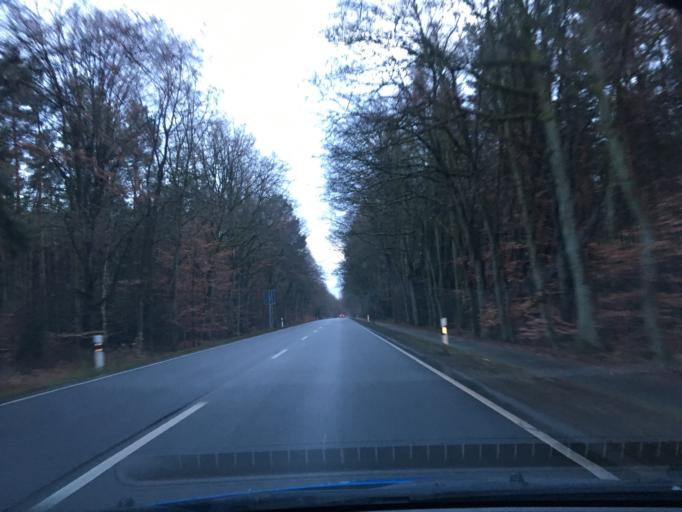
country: DE
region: Lower Saxony
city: Suderburg
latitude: 52.8839
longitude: 10.5038
